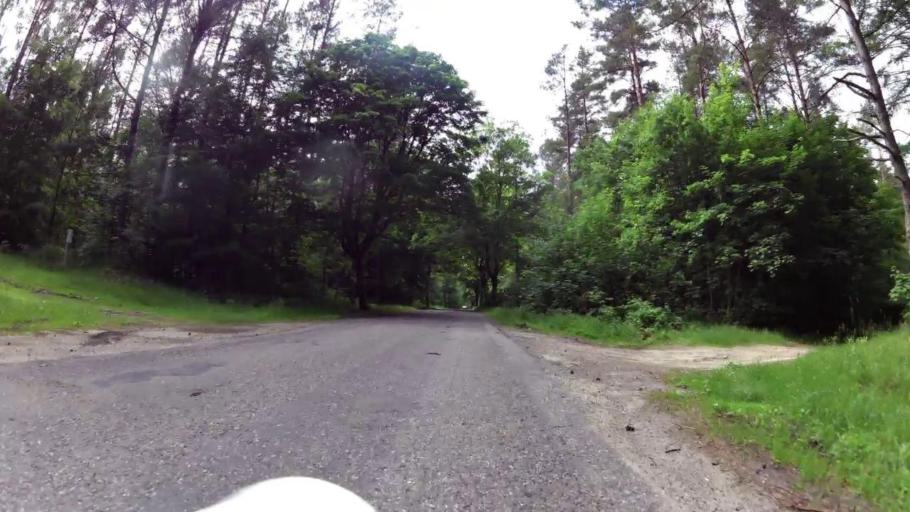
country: PL
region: West Pomeranian Voivodeship
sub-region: Powiat szczecinecki
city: Bialy Bor
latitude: 53.9565
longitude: 16.7456
